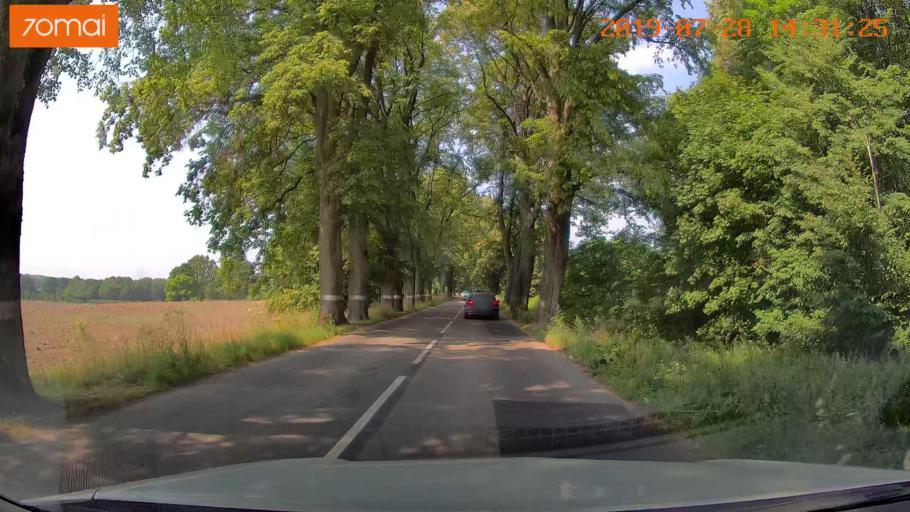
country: RU
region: Kaliningrad
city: Primorsk
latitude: 54.8064
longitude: 20.0513
